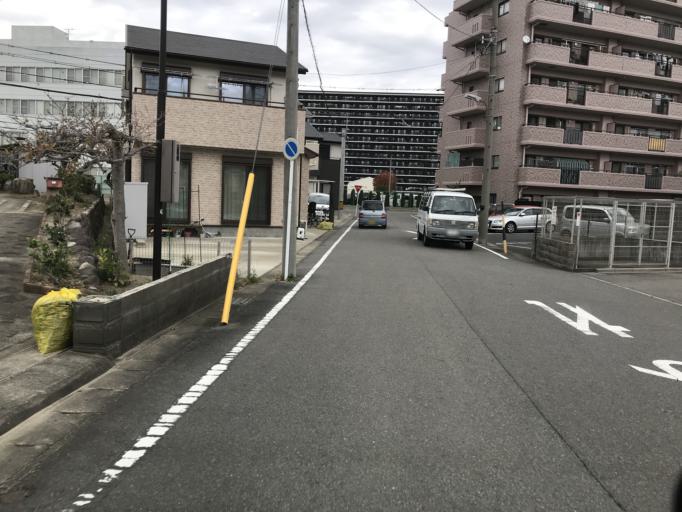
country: JP
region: Aichi
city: Nagoya-shi
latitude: 35.1949
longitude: 136.8585
